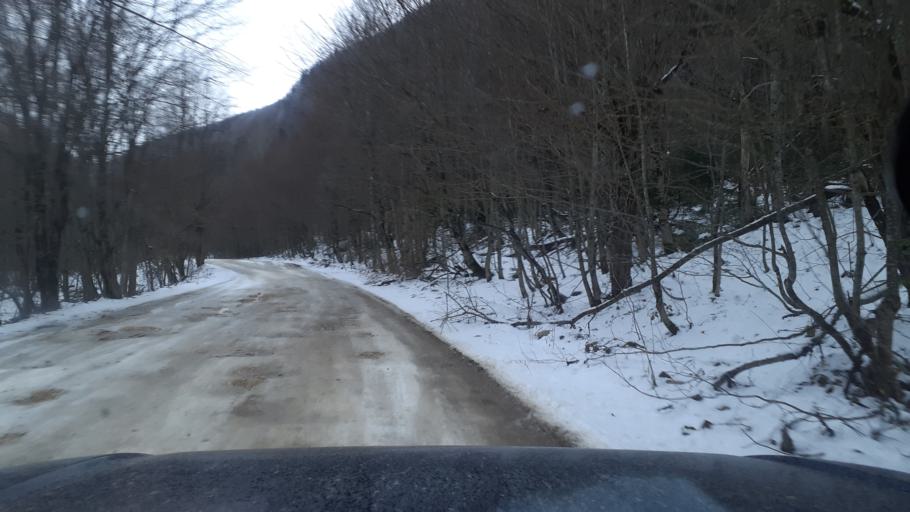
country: RU
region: Krasnodarskiy
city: Neftegorsk
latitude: 44.0817
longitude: 39.8082
